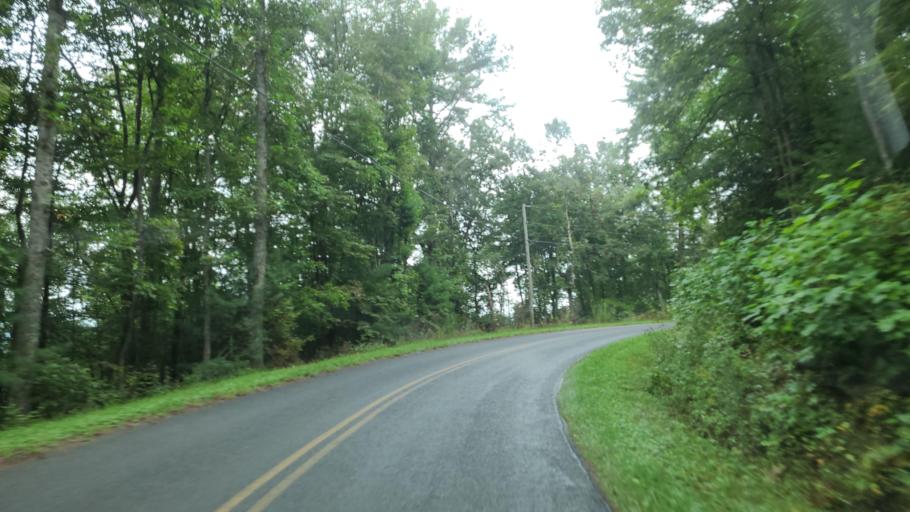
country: US
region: Georgia
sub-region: Gilmer County
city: Ellijay
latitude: 34.7964
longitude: -84.5627
